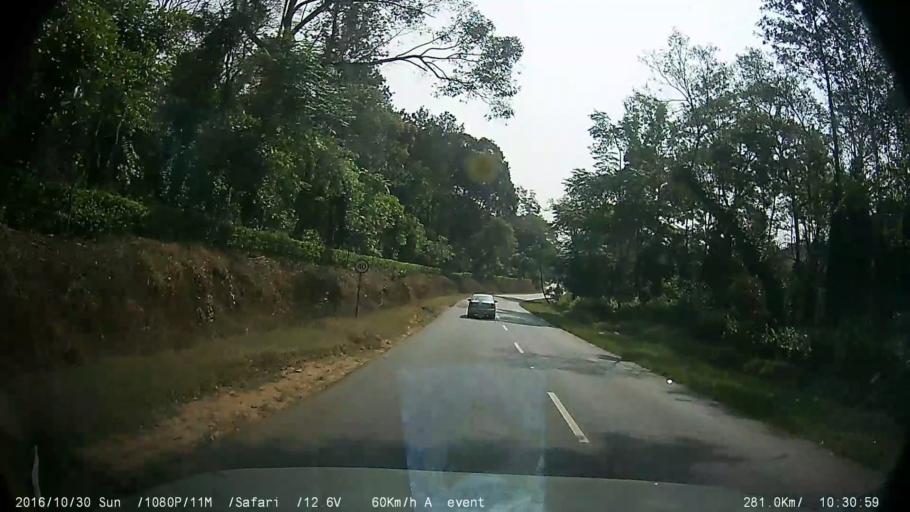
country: IN
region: Karnataka
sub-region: Kodagu
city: Suntikoppa
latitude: 12.4470
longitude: 75.8159
